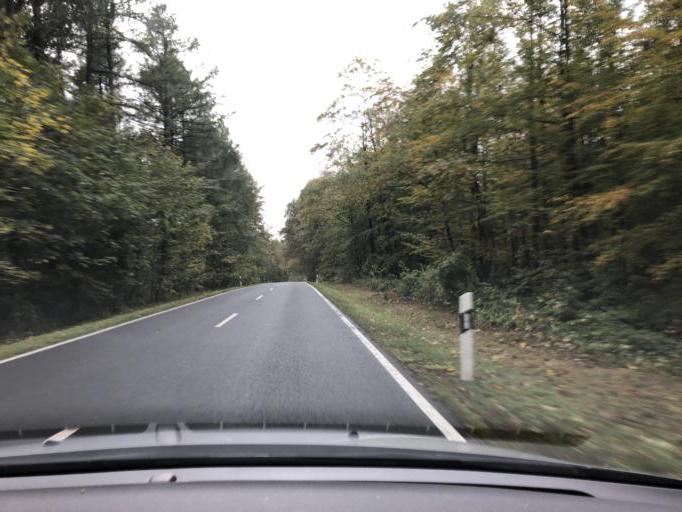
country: DE
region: Thuringia
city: Wachstedt
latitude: 51.2849
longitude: 10.2281
